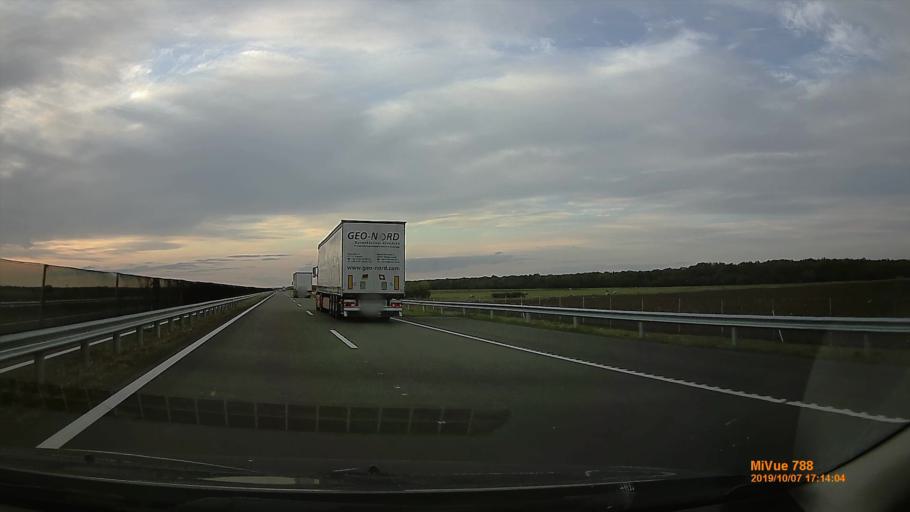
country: HU
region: Jasz-Nagykun-Szolnok
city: Kunszentmarton
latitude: 46.8283
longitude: 20.3582
